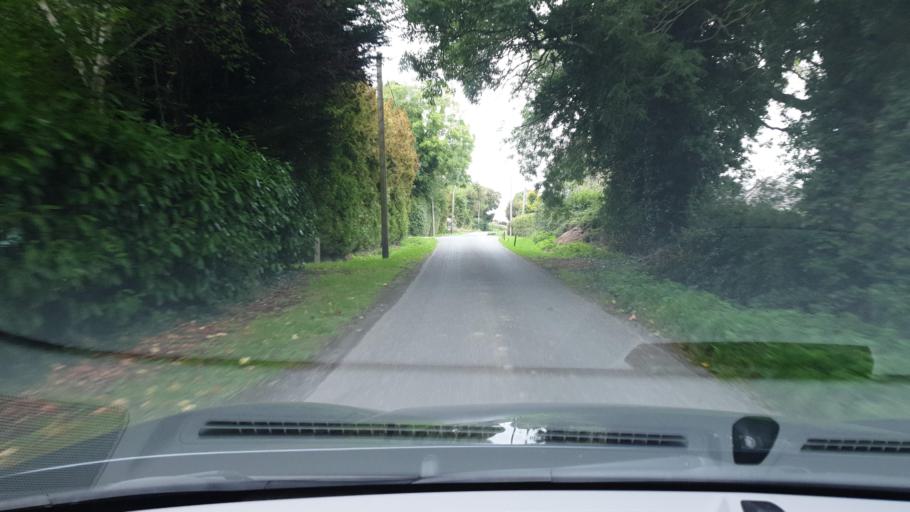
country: IE
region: Leinster
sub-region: An Mhi
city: Ratoath
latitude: 53.5059
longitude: -6.4877
